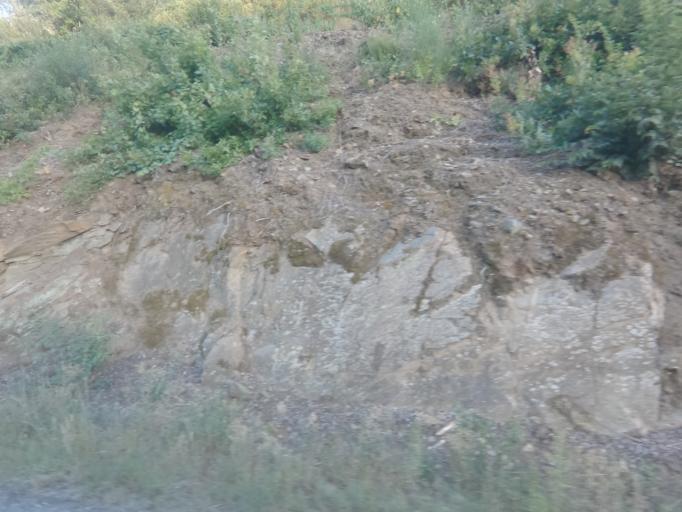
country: PT
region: Viseu
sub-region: Armamar
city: Armamar
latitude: 41.1714
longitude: -7.6841
